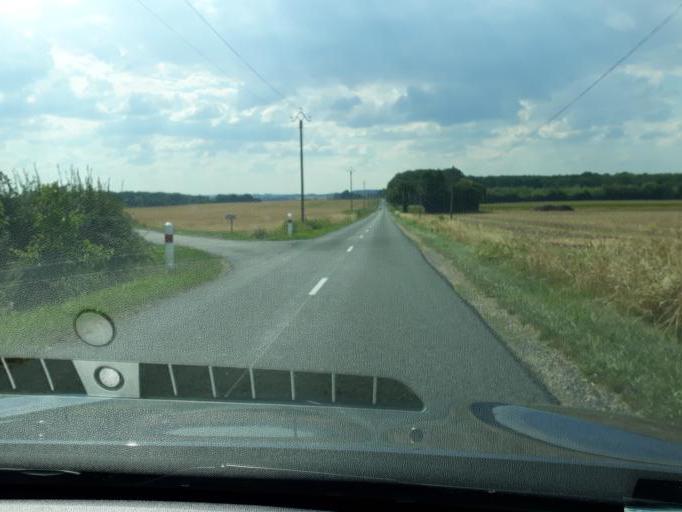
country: FR
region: Centre
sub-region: Departement du Cher
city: Nerondes
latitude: 47.0489
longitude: 2.8651
